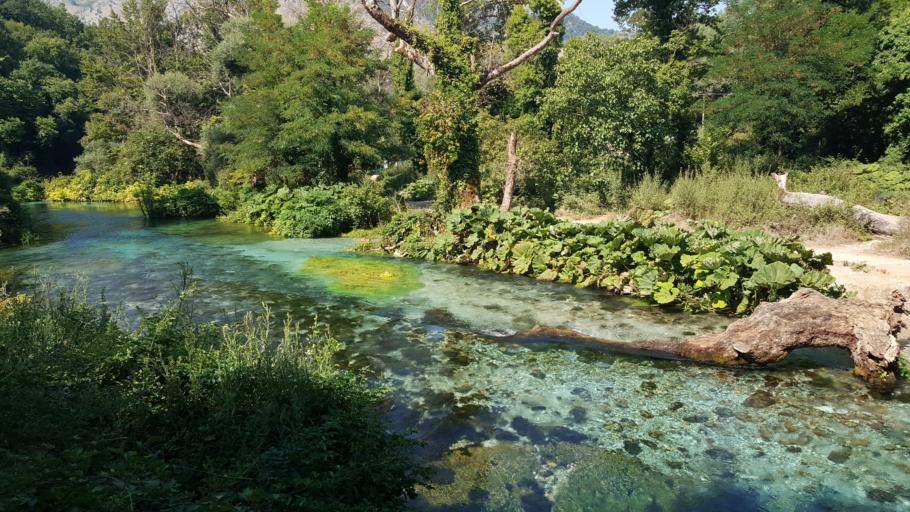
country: AL
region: Vlore
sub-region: Rrethi i Sarandes
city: Dhiver
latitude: 39.9239
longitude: 20.1928
